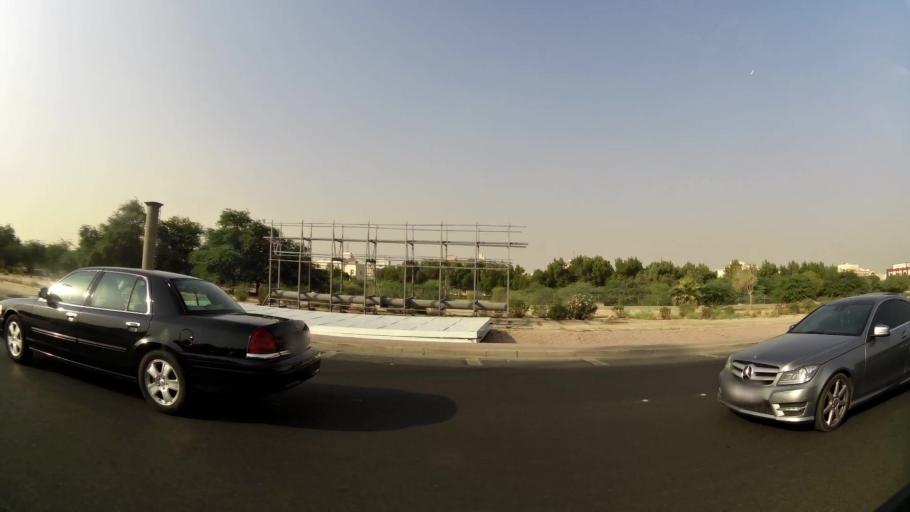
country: KW
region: Muhafazat Hawalli
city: Salwa
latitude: 29.2744
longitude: 48.0819
